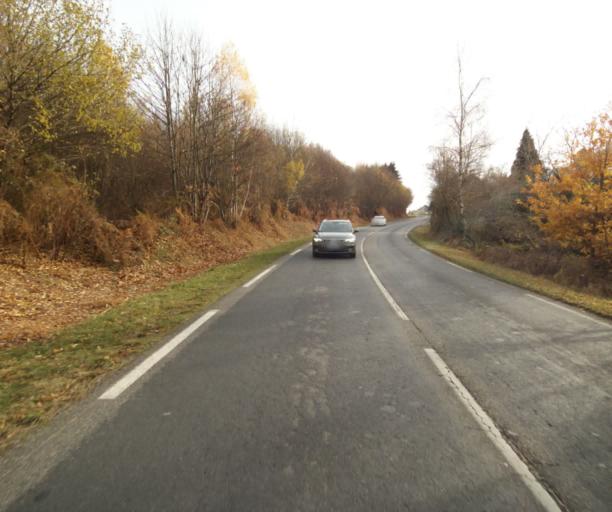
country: FR
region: Limousin
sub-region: Departement de la Correze
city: Sainte-Fortunade
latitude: 45.1998
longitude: 1.7728
